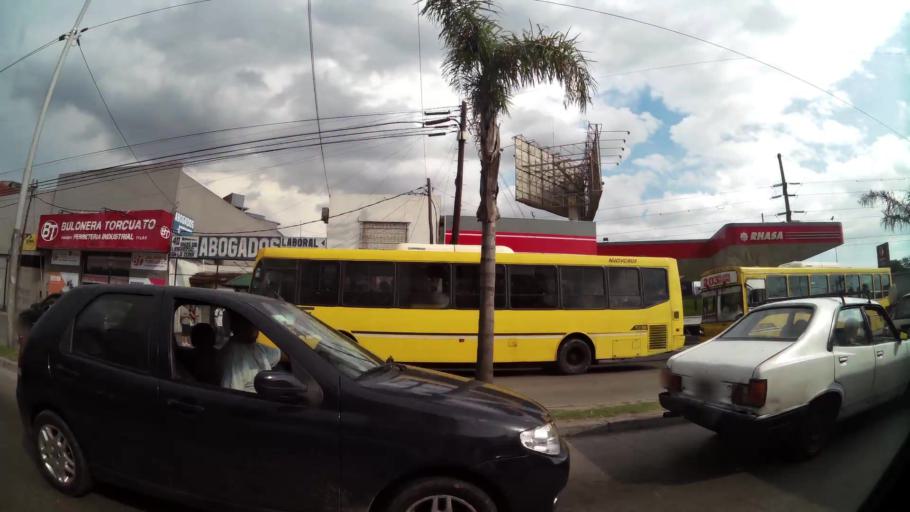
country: AR
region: Buenos Aires
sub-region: Partido de Tigre
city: Tigre
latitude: -34.4847
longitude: -58.6135
